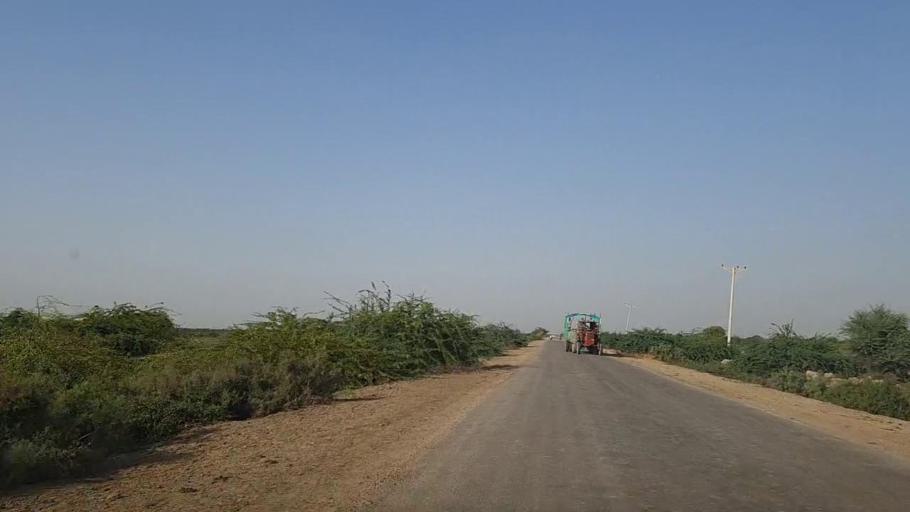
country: PK
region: Sindh
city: Mirpur Batoro
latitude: 24.6001
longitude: 68.4006
